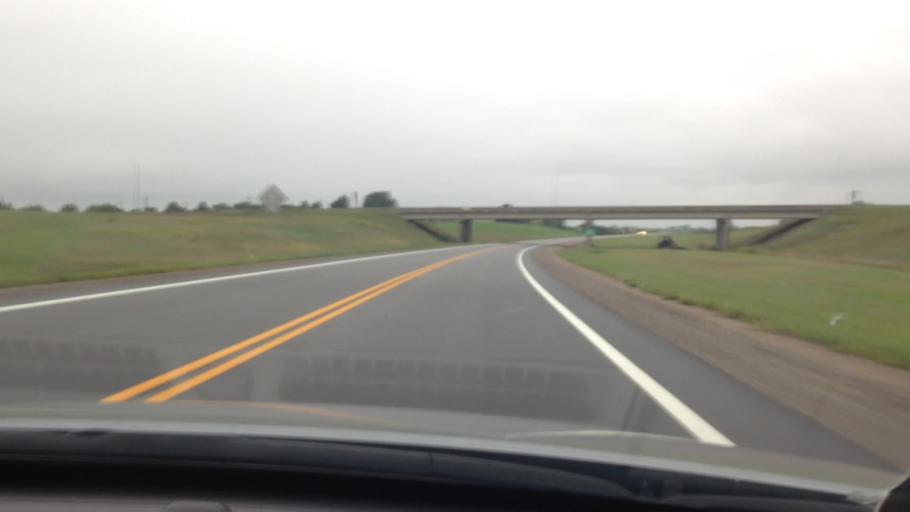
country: US
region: Kansas
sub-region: Brown County
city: Hiawatha
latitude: 39.8415
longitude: -95.5247
